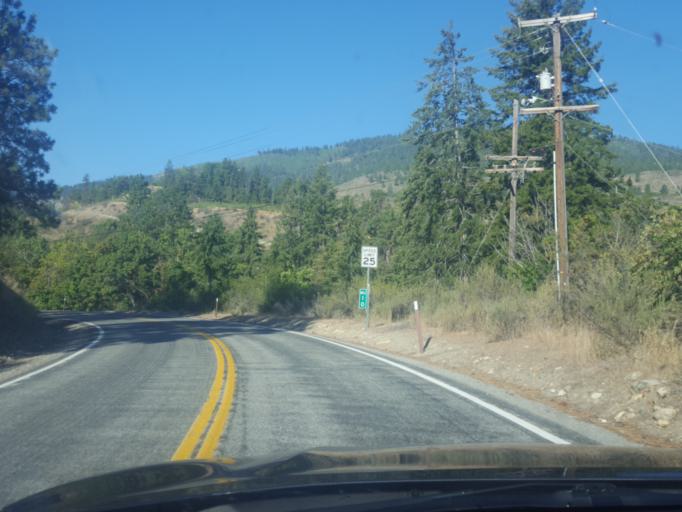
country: US
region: Washington
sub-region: Chelan County
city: Granite Falls
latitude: 47.9922
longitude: -120.2602
